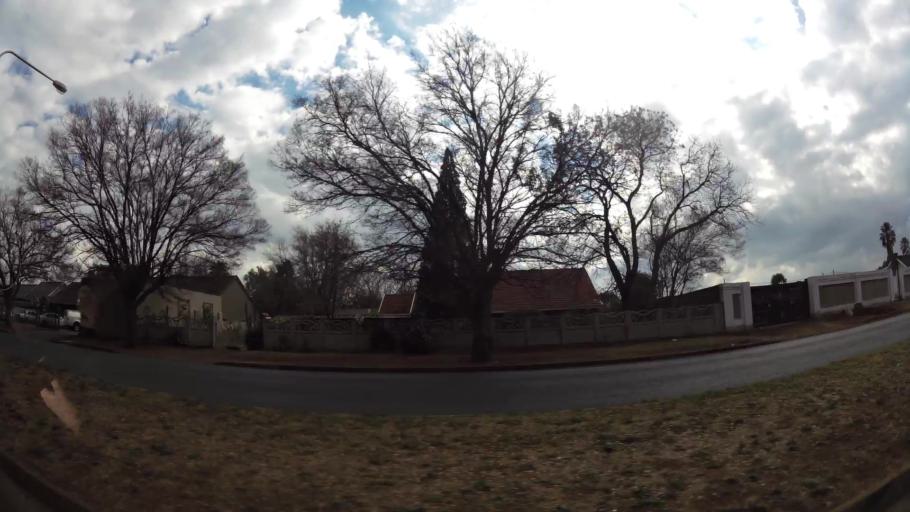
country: ZA
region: Gauteng
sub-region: Sedibeng District Municipality
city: Vereeniging
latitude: -26.6572
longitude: 27.9927
